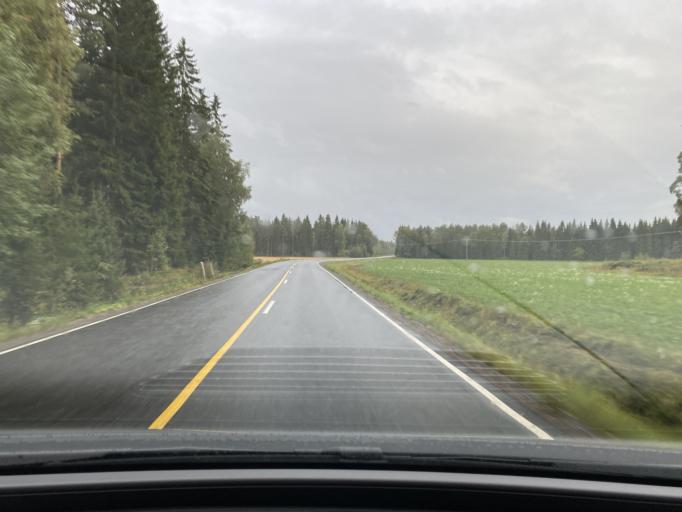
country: FI
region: Varsinais-Suomi
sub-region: Loimaa
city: Alastaro
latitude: 61.0038
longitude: 22.9476
